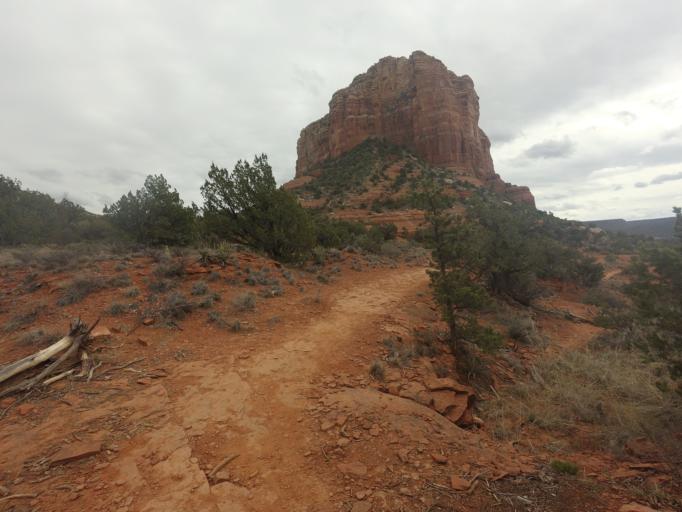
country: US
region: Arizona
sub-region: Yavapai County
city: Village of Oak Creek (Big Park)
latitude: 34.8030
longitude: -111.7621
